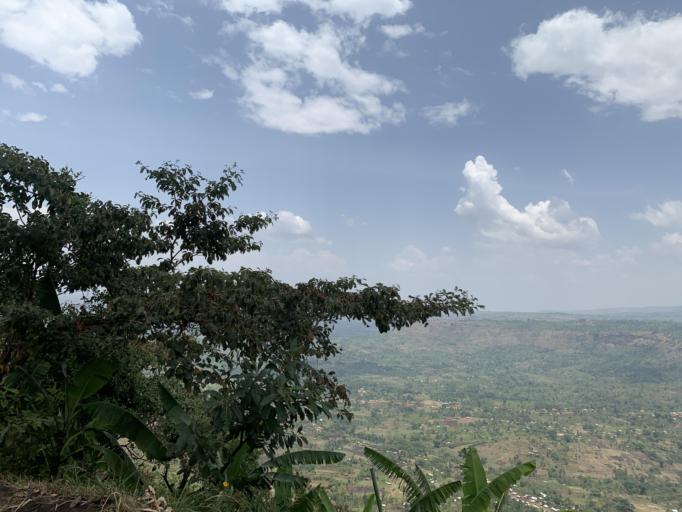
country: UG
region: Eastern Region
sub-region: Sironko District
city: Sironko
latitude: 1.2614
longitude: 34.3029
